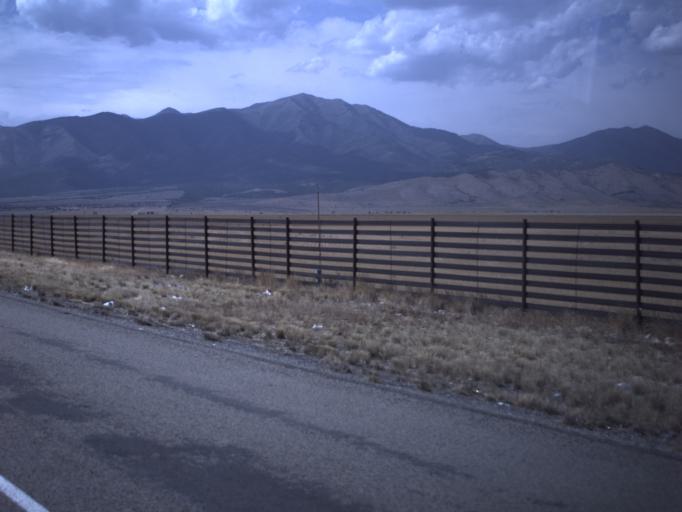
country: US
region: Utah
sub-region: Utah County
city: Eagle Mountain
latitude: 40.3634
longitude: -112.0432
